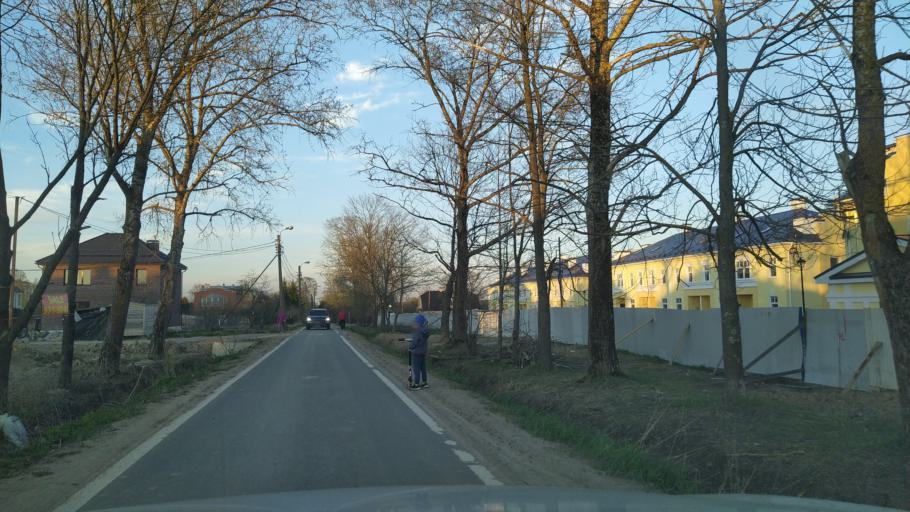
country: RU
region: St.-Petersburg
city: Pavlovsk
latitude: 59.6914
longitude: 30.4107
